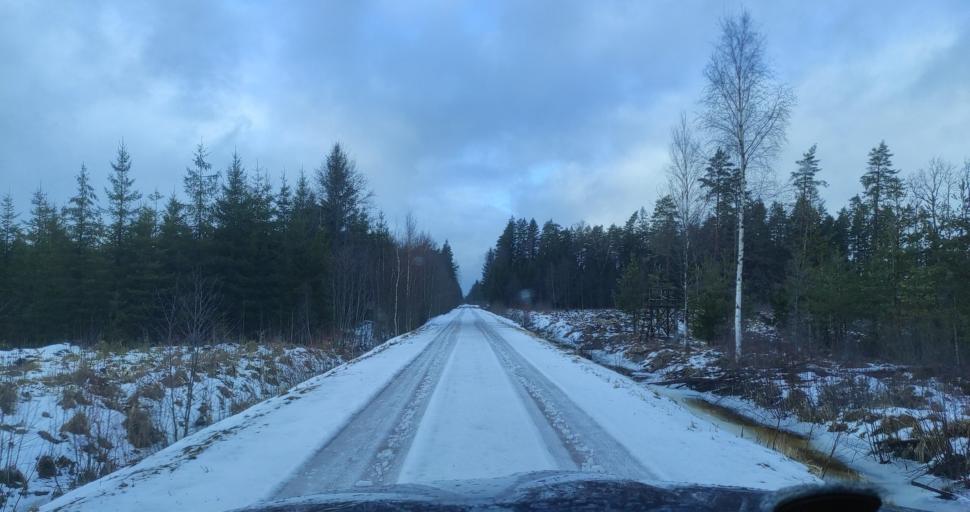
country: LV
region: Dundaga
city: Dundaga
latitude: 57.4097
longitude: 22.0848
